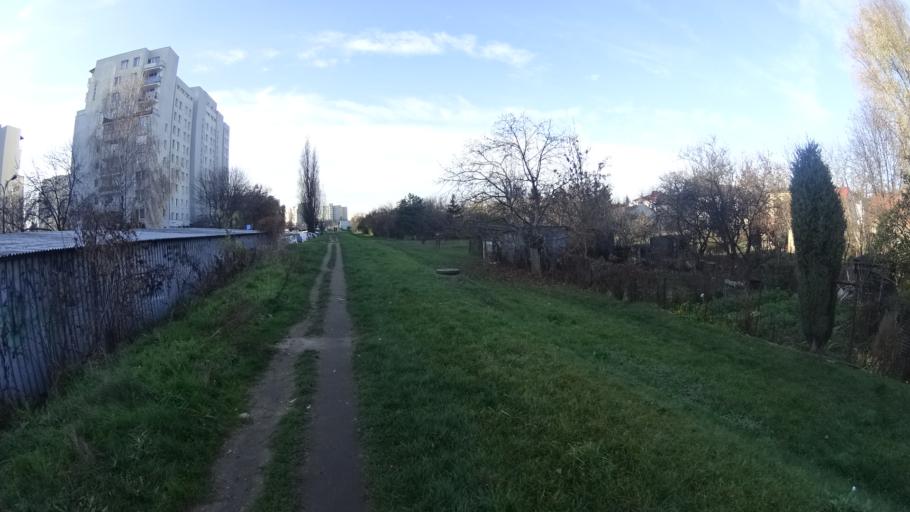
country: PL
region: Masovian Voivodeship
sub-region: Warszawa
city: Targowek
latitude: 52.2761
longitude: 21.0624
